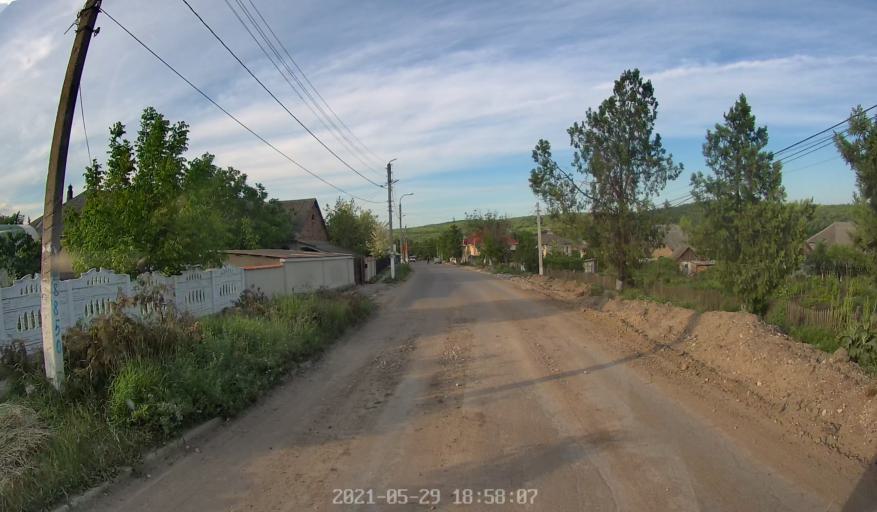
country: MD
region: Chisinau
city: Singera
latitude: 46.8247
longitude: 28.9703
